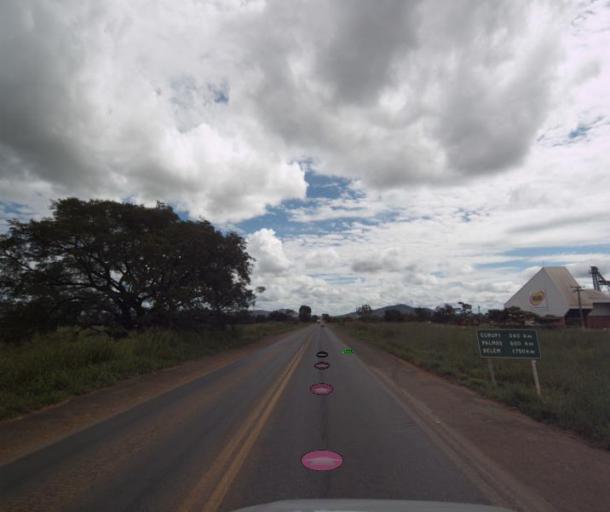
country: BR
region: Goias
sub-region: Uruacu
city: Uruacu
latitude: -14.4675
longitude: -49.1561
